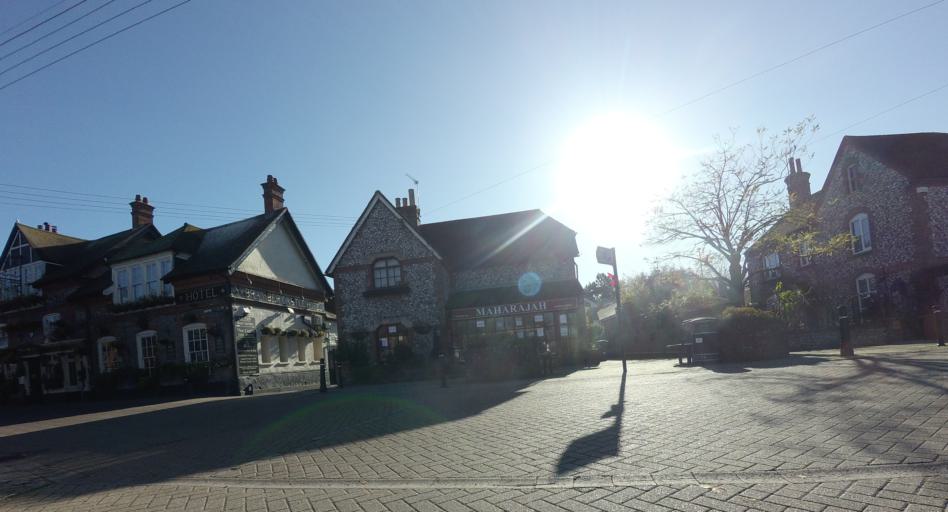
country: GB
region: England
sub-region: West Sussex
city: Steyning
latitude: 50.8830
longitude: -0.3121
